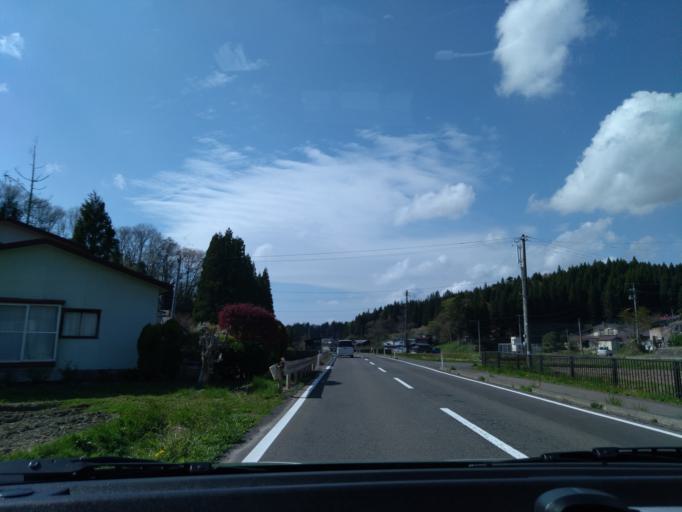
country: JP
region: Akita
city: Akita
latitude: 39.7098
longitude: 140.2049
